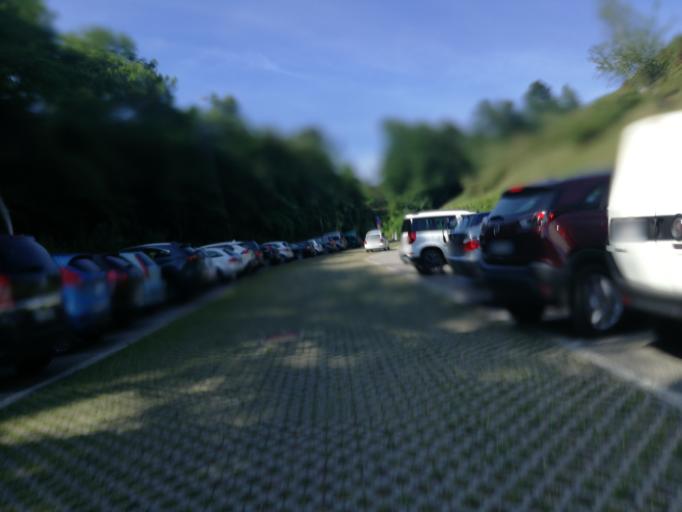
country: IT
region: Lombardy
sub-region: Provincia di Bergamo
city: Villa d'Adda
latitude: 45.7074
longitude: 9.4557
